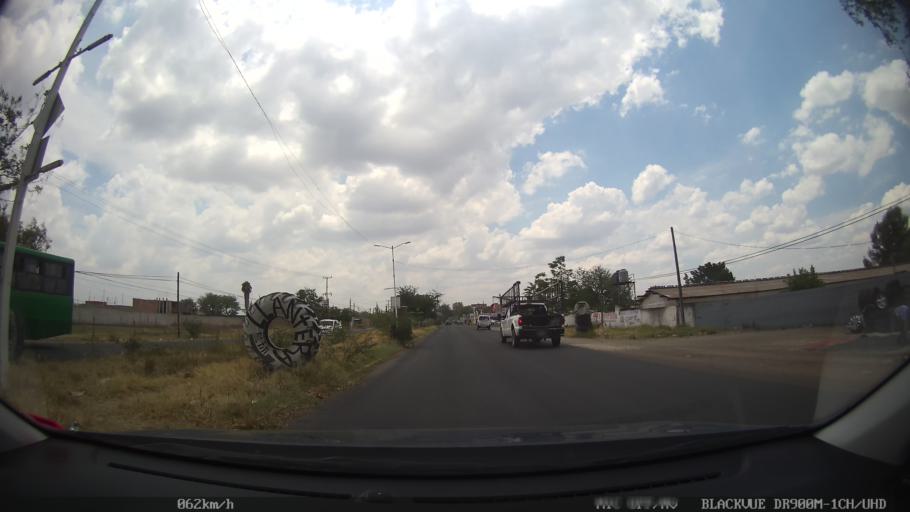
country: MX
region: Jalisco
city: Tonala
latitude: 20.6694
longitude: -103.2305
